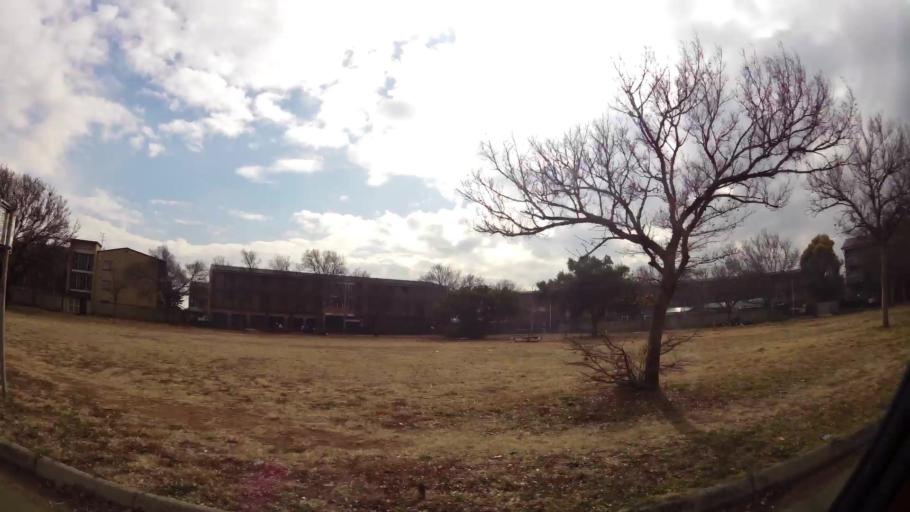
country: ZA
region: Gauteng
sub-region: Sedibeng District Municipality
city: Vanderbijlpark
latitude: -26.6932
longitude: 27.8401
